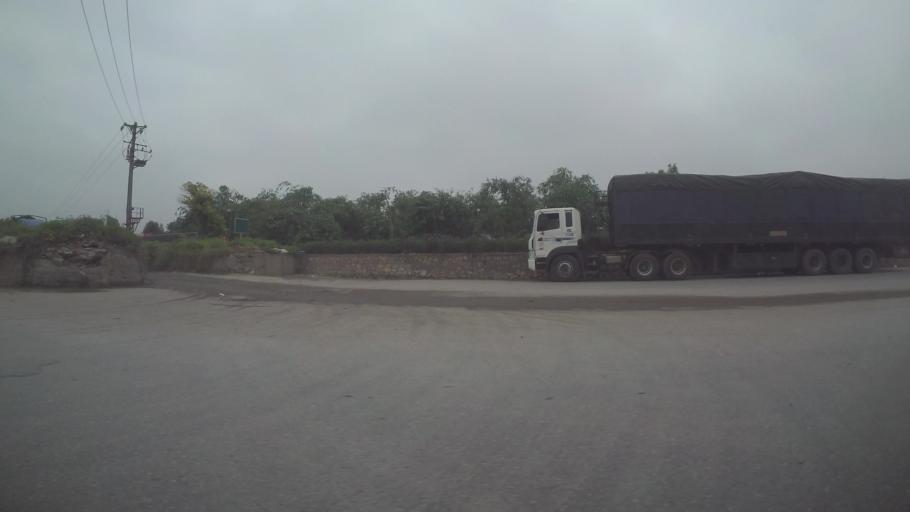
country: VN
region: Ha Noi
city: Trau Quy
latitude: 20.9850
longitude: 105.8950
